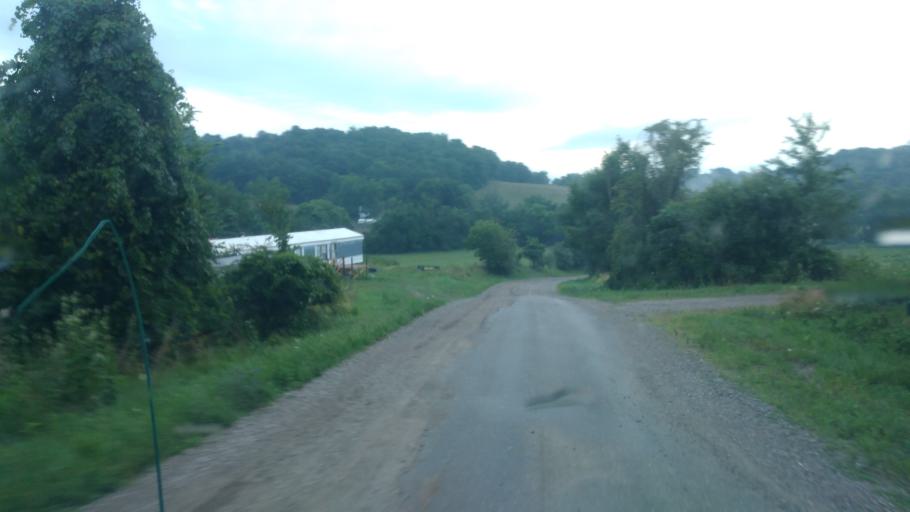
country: US
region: Ohio
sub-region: Guernsey County
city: Byesville
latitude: 40.0237
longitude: -81.3606
